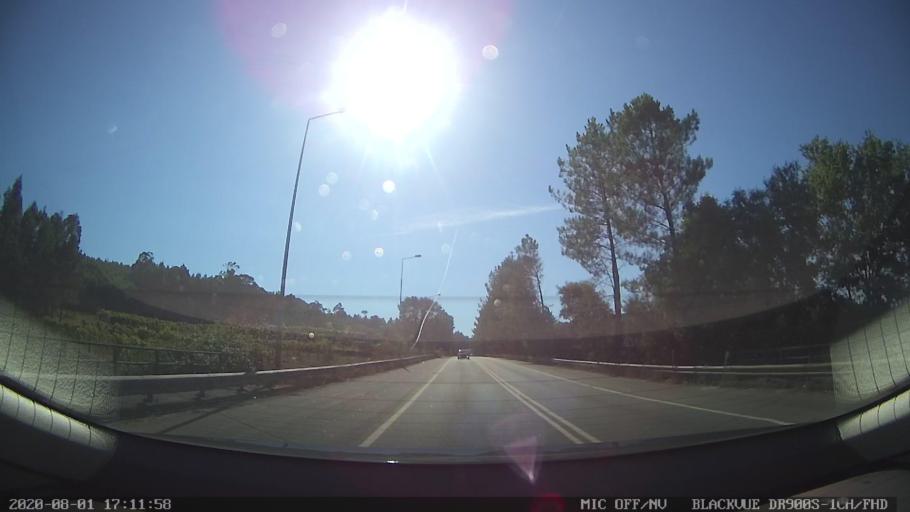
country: PT
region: Braga
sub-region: Vila Nova de Famalicao
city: Ferreiros
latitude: 41.3399
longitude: -8.5149
